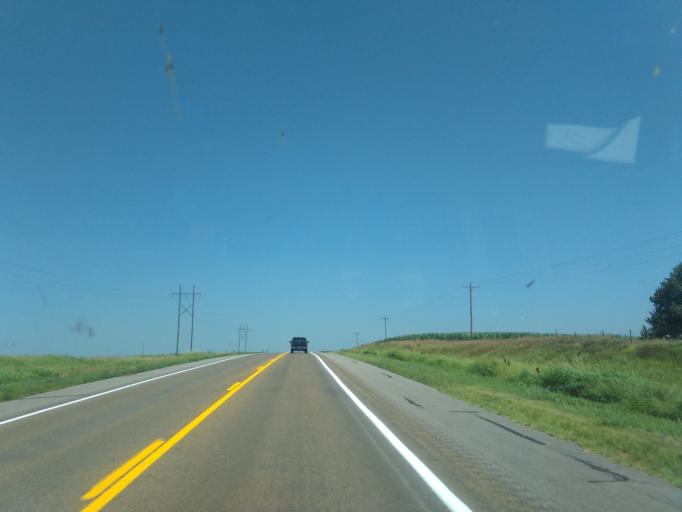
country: US
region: Nebraska
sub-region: Lincoln County
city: North Platte
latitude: 40.8014
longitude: -100.7538
